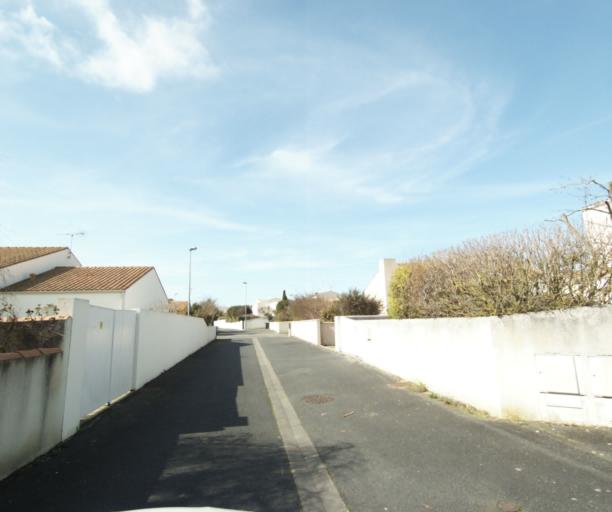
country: FR
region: Poitou-Charentes
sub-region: Departement de la Charente-Maritime
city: Lagord
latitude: 46.1835
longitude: -1.1641
